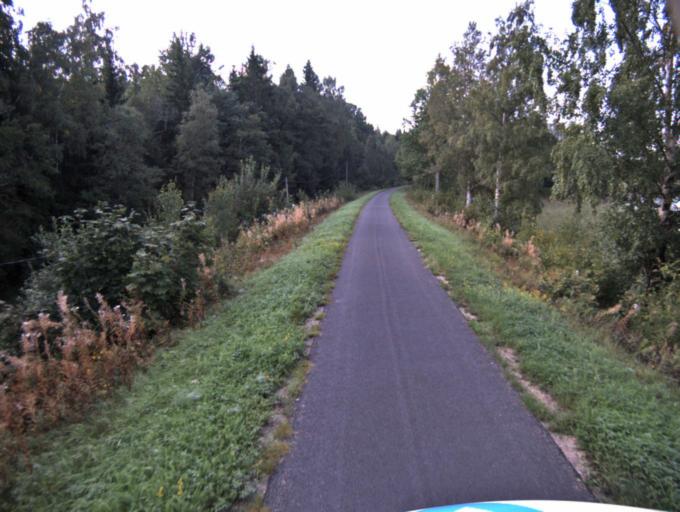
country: SE
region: Vaestra Goetaland
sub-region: Ulricehamns Kommun
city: Ulricehamn
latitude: 57.6972
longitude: 13.3927
